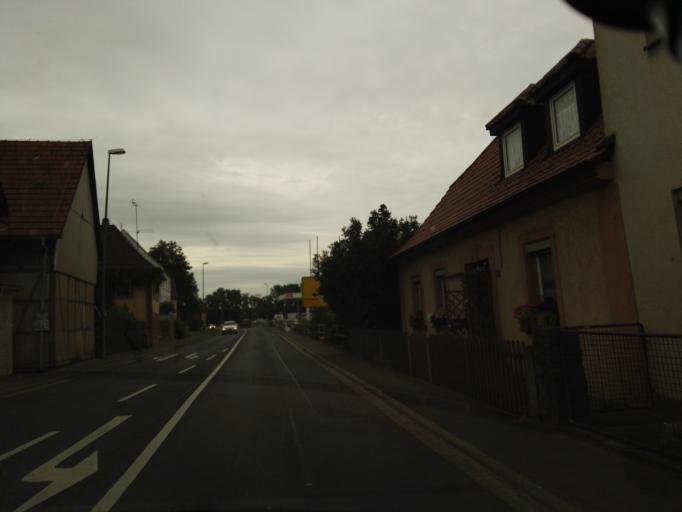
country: DE
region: Bavaria
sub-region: Upper Franconia
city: Burgkunstadt
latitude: 50.1451
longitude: 11.2302
